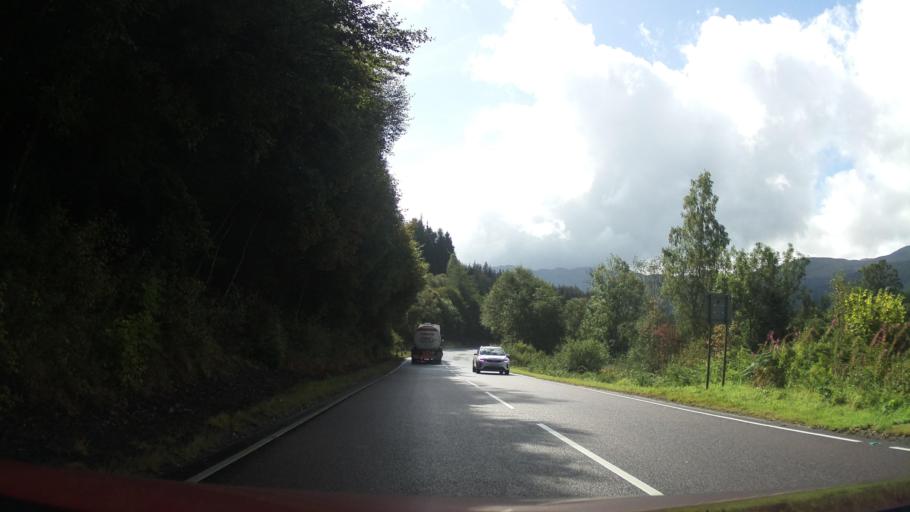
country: GB
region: Scotland
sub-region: Stirling
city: Callander
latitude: 56.3355
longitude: -4.3243
